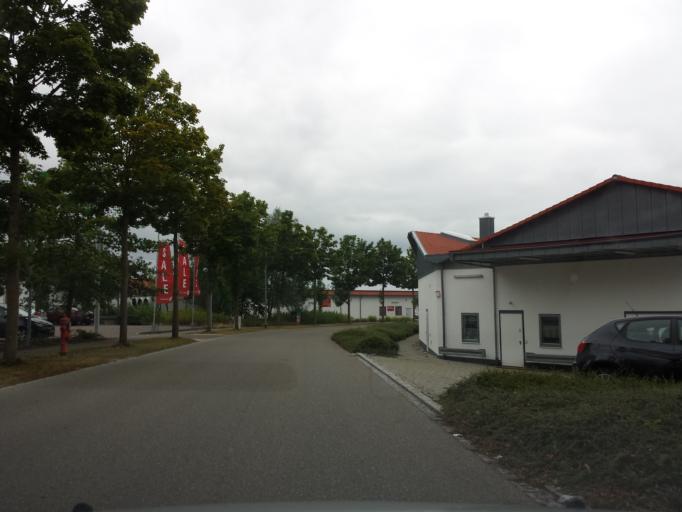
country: DE
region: Bavaria
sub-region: Swabia
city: Wasserburg
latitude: 48.4514
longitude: 10.2594
